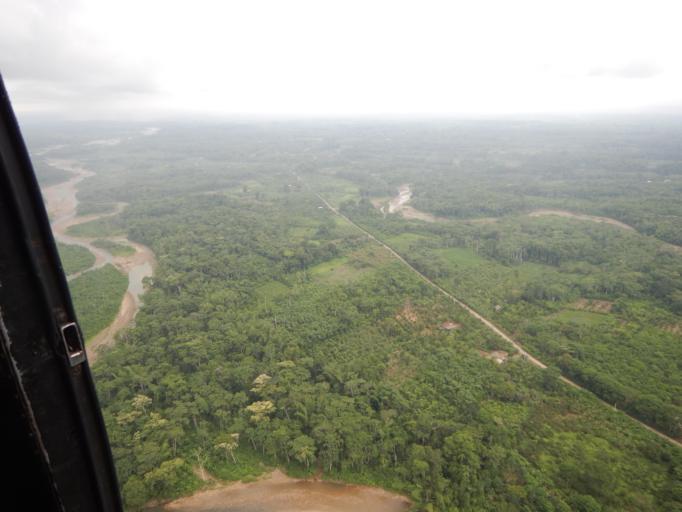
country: BO
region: Cochabamba
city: Chimore
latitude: -17.2386
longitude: -64.6482
